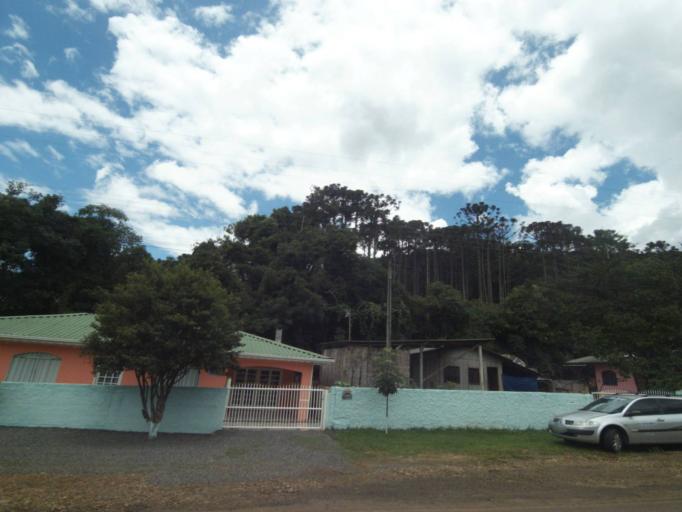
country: BR
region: Parana
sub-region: Pinhao
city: Pinhao
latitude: -26.1572
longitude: -51.5674
